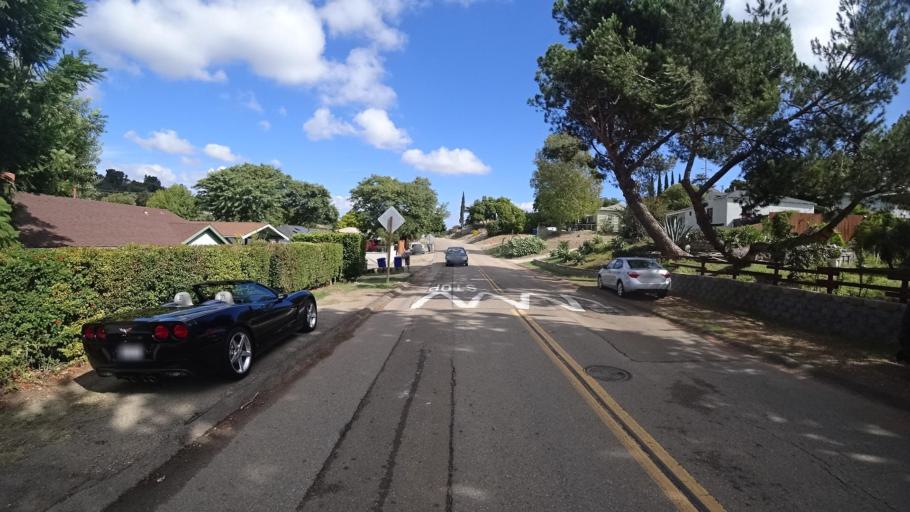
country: US
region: California
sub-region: San Diego County
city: Casa de Oro-Mount Helix
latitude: 32.7427
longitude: -116.9711
